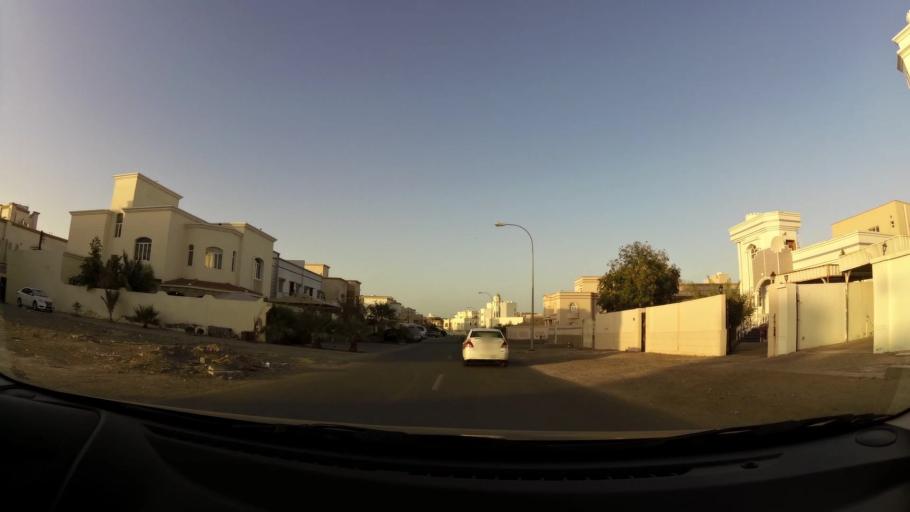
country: OM
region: Muhafazat Masqat
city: As Sib al Jadidah
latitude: 23.6016
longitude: 58.2293
